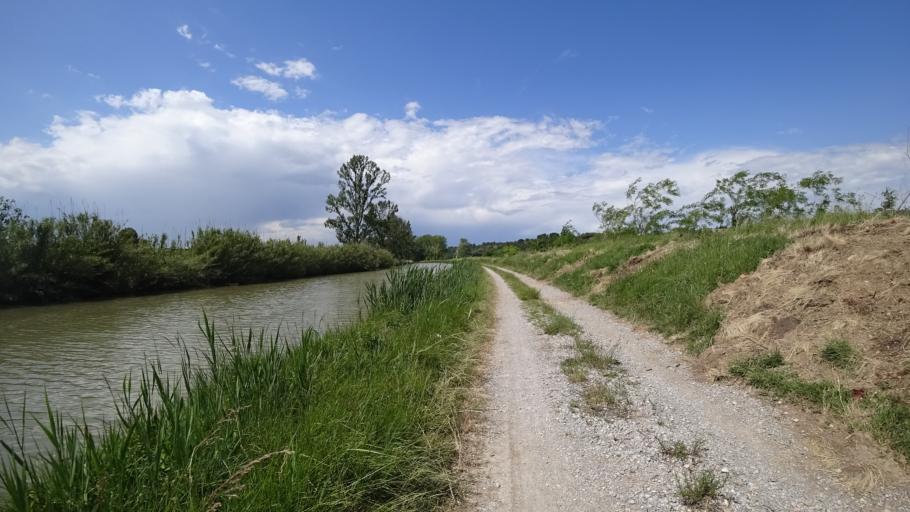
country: FR
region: Languedoc-Roussillon
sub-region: Departement de l'Aude
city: Canet
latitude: 43.2494
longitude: 2.8398
